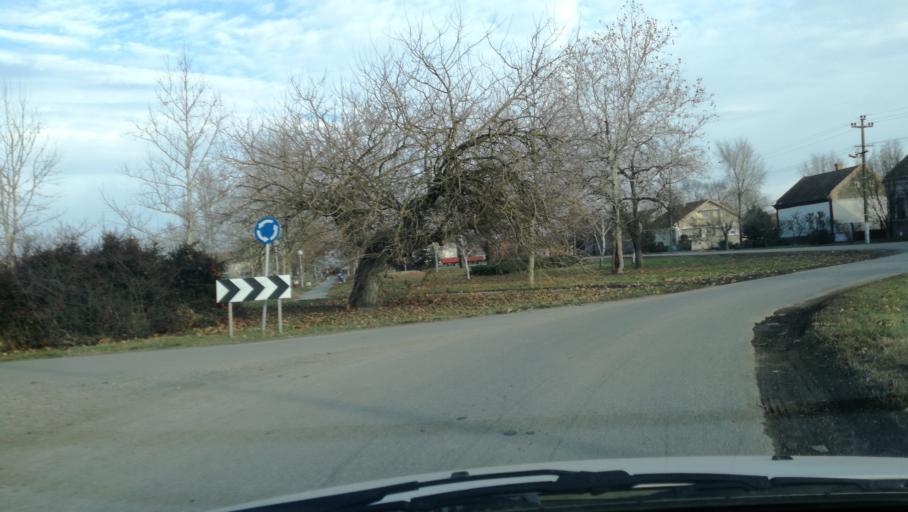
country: RS
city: Novi Kozarci
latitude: 45.7770
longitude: 20.6052
